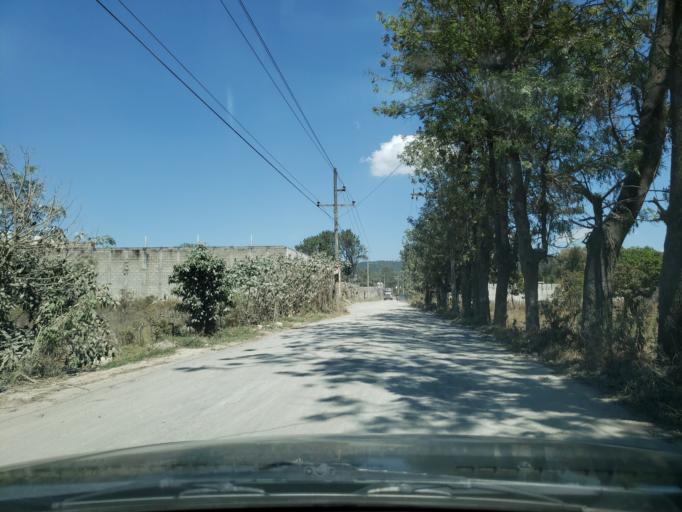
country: GT
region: Chimaltenango
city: El Tejar
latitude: 14.6495
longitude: -90.8020
